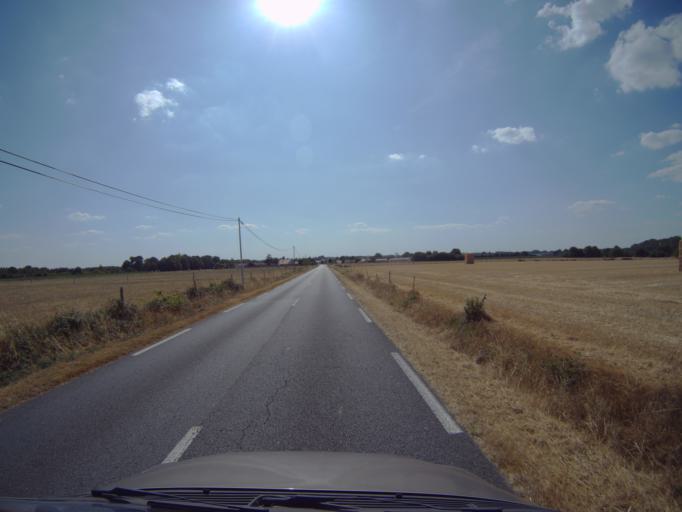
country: FR
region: Pays de la Loire
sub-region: Departement de la Loire-Atlantique
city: Montbert
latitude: 47.0581
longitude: -1.4702
